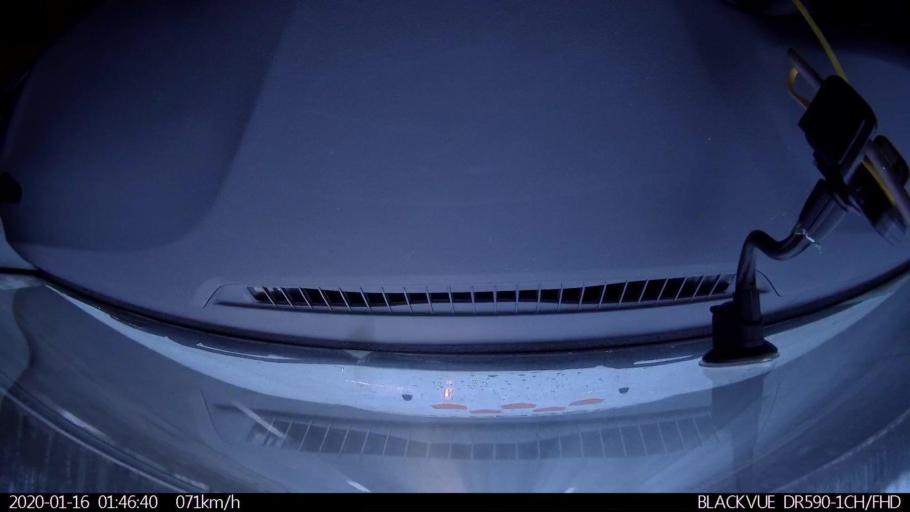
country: RU
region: Nizjnij Novgorod
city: Gorbatovka
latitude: 56.3103
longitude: 43.7863
